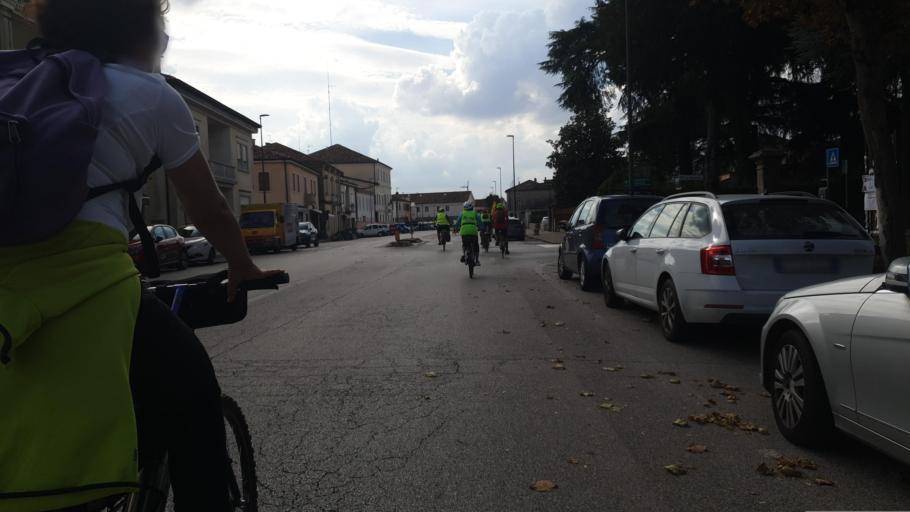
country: IT
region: Veneto
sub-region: Provincia di Vicenza
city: Noventa Vicentina
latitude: 45.2917
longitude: 11.5428
